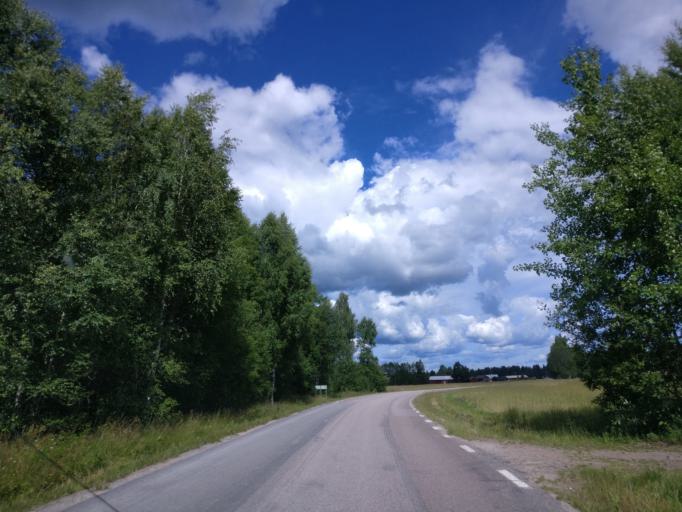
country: SE
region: Vaermland
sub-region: Hagfors Kommun
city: Ekshaerad
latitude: 60.0423
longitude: 13.4939
